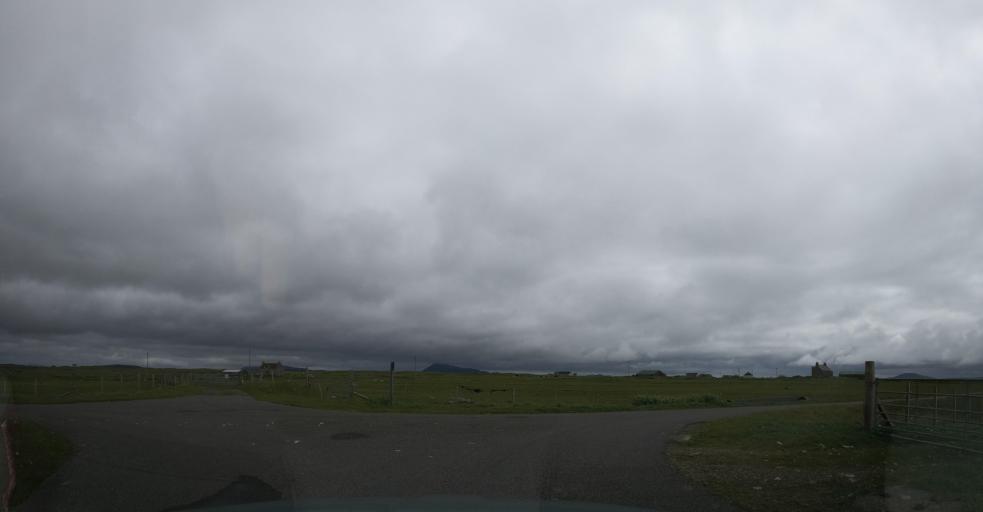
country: GB
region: Scotland
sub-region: Eilean Siar
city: Isle of North Uist
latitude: 57.5308
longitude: -7.3682
